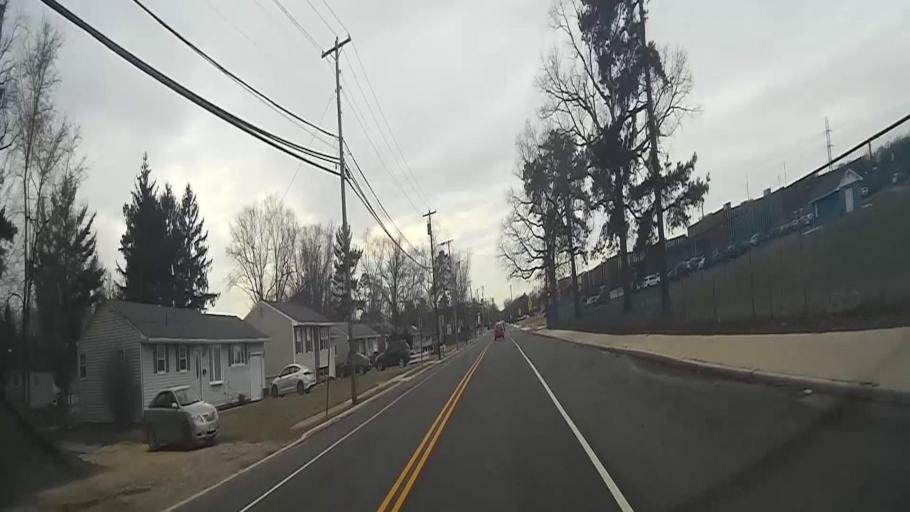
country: US
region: New Jersey
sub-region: Camden County
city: Pine Hill
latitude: 39.7764
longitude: -74.9638
